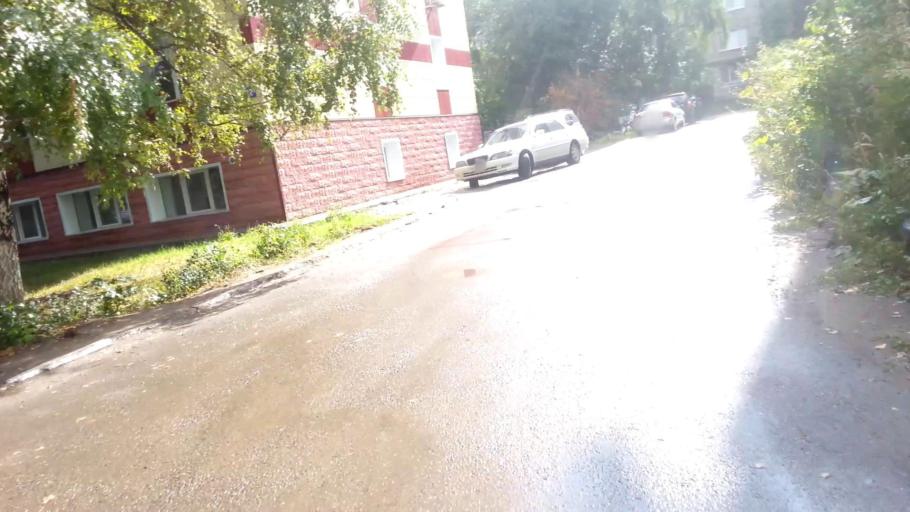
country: RU
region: Altai Krai
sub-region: Gorod Barnaulskiy
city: Barnaul
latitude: 53.3482
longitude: 83.7579
